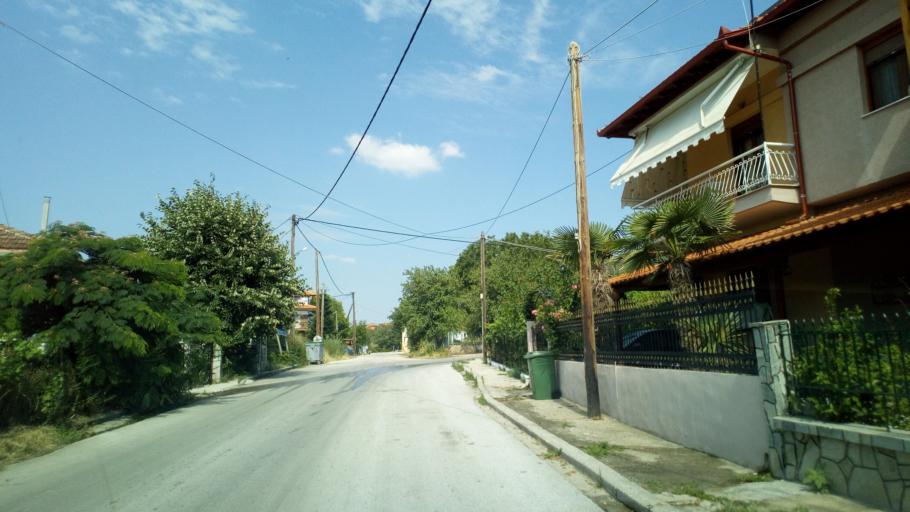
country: GR
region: Central Macedonia
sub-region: Nomos Thessalonikis
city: Sochos
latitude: 40.8140
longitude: 23.3562
